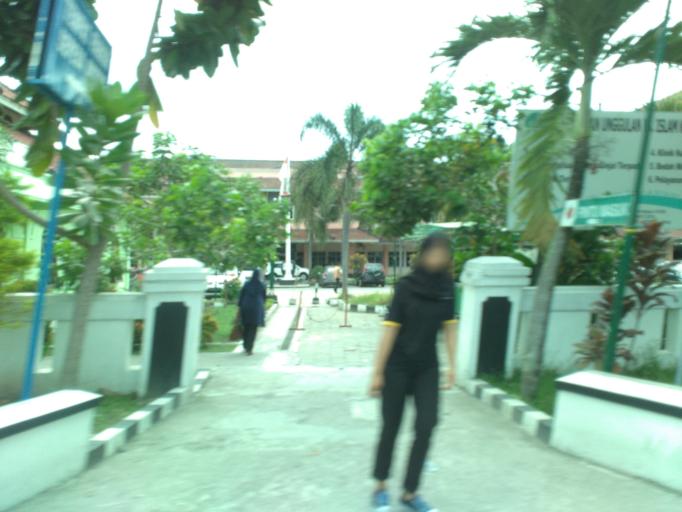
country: ID
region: Central Java
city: Klaten
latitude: -7.6858
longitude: 110.6349
